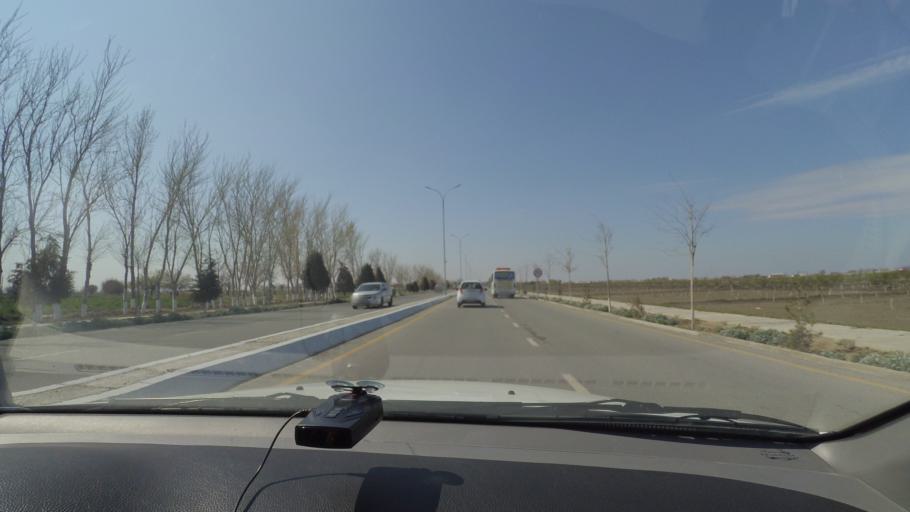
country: UZ
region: Bukhara
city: Bukhara
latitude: 39.7984
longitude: 64.4836
